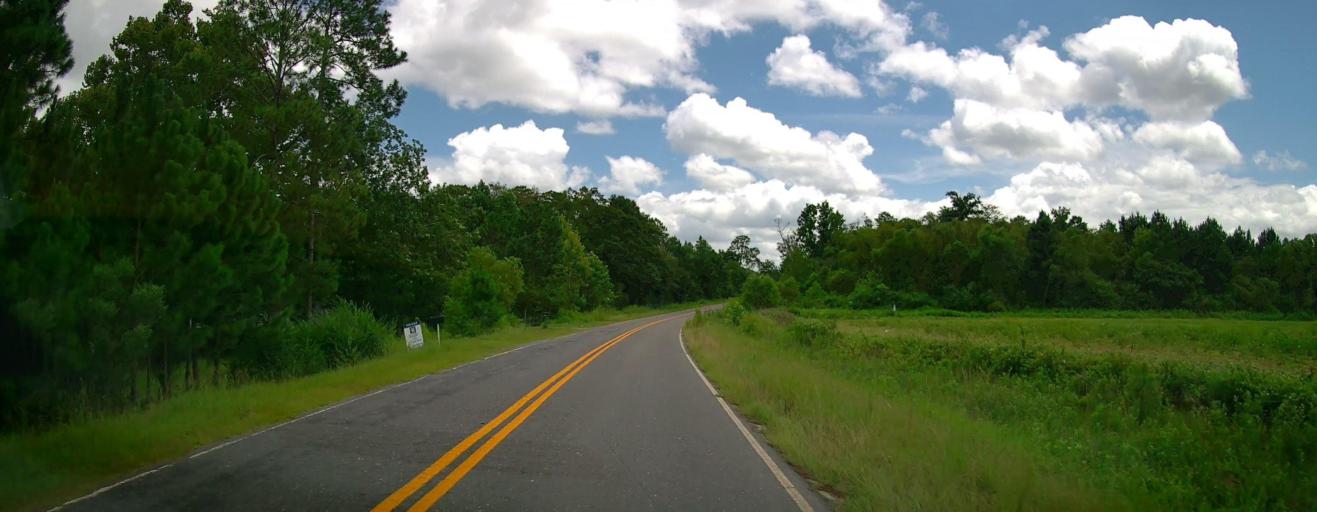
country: US
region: Georgia
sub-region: Irwin County
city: Ocilla
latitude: 31.6483
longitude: -83.3987
